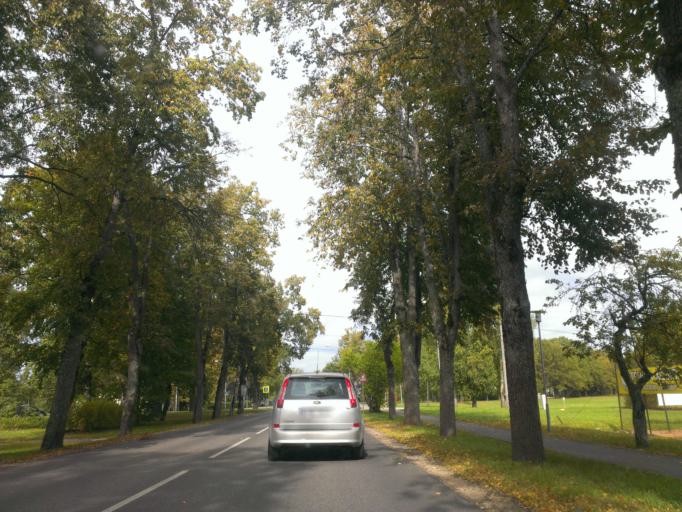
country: LV
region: Sigulda
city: Sigulda
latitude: 57.1581
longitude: 24.8535
